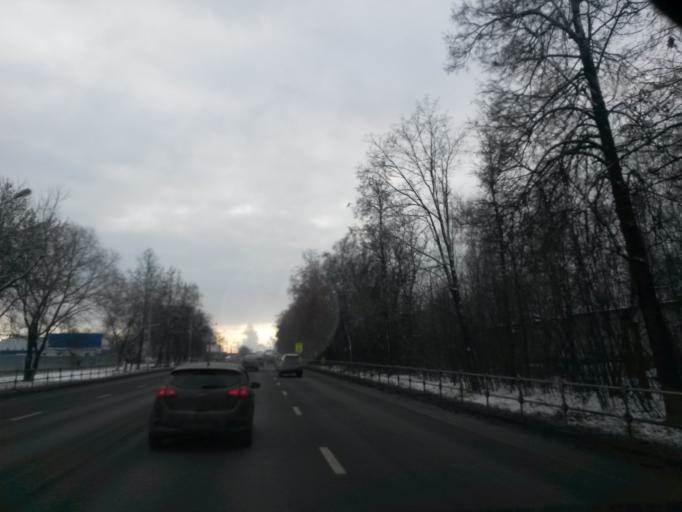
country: RU
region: Moskovskaya
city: Klimovsk
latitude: 55.3713
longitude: 37.5322
